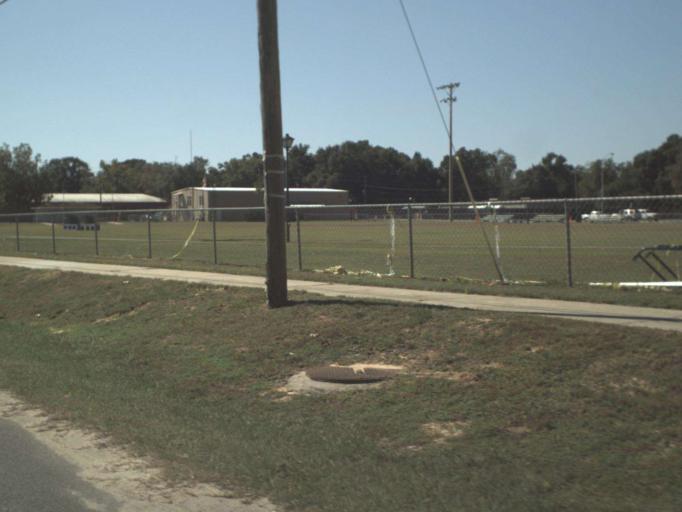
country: US
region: Florida
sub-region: Walton County
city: DeFuniak Springs
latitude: 30.7272
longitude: -86.1149
